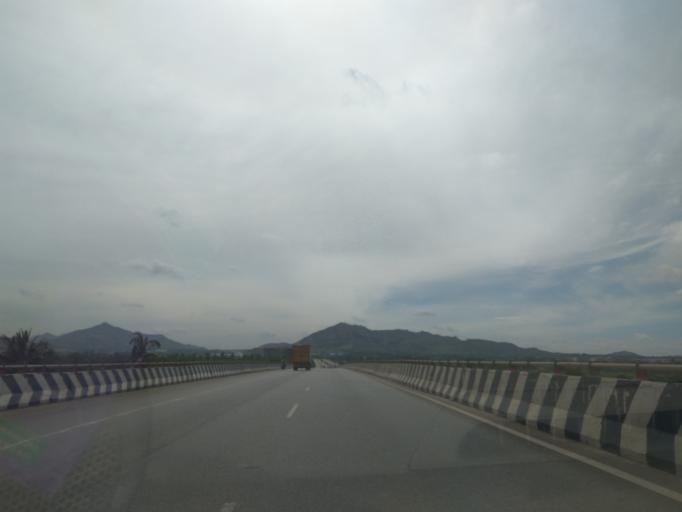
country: IN
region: Karnataka
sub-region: Kolar
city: Malur
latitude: 13.1320
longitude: 77.9826
